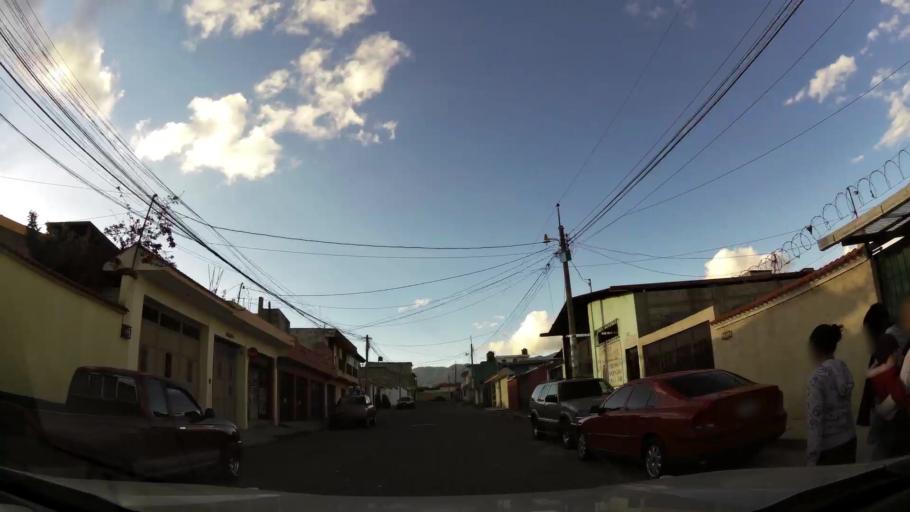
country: GT
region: Quetzaltenango
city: Quetzaltenango
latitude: 14.8547
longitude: -91.5325
